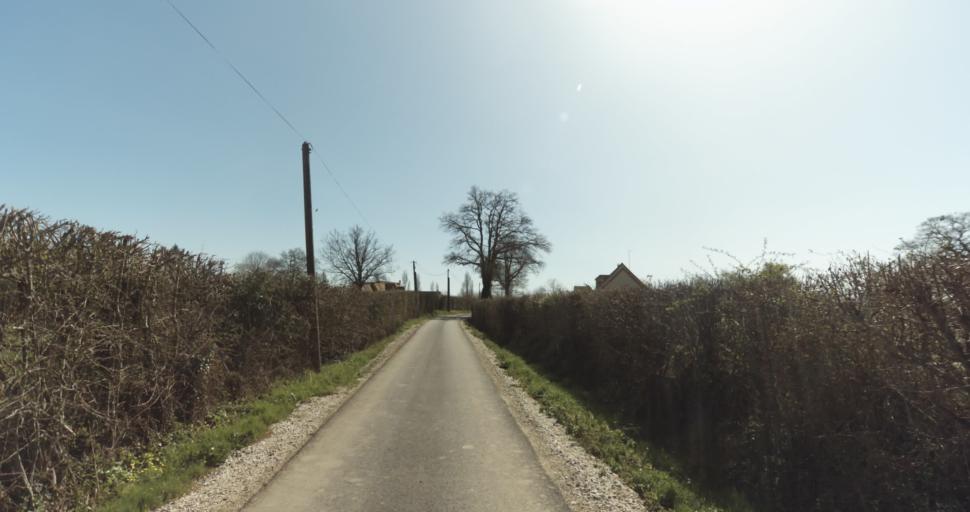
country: FR
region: Lower Normandy
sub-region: Departement du Calvados
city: Saint-Pierre-sur-Dives
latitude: 49.0064
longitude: 0.0006
